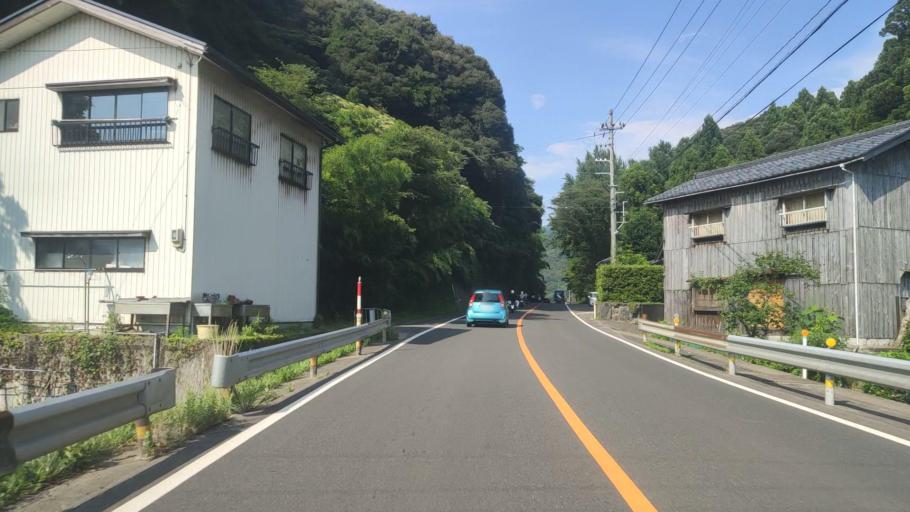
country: JP
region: Fukui
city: Tsuruga
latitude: 35.7057
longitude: 136.0844
